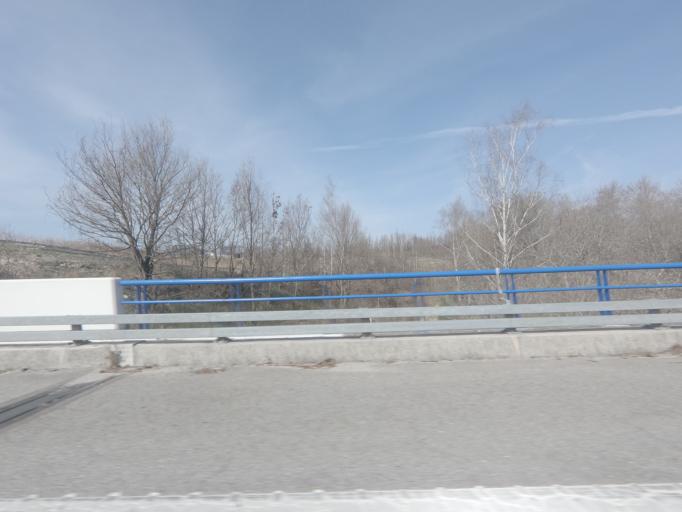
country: PT
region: Viseu
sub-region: Oliveira de Frades
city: Oliveira de Frades
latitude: 40.6854
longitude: -8.2196
